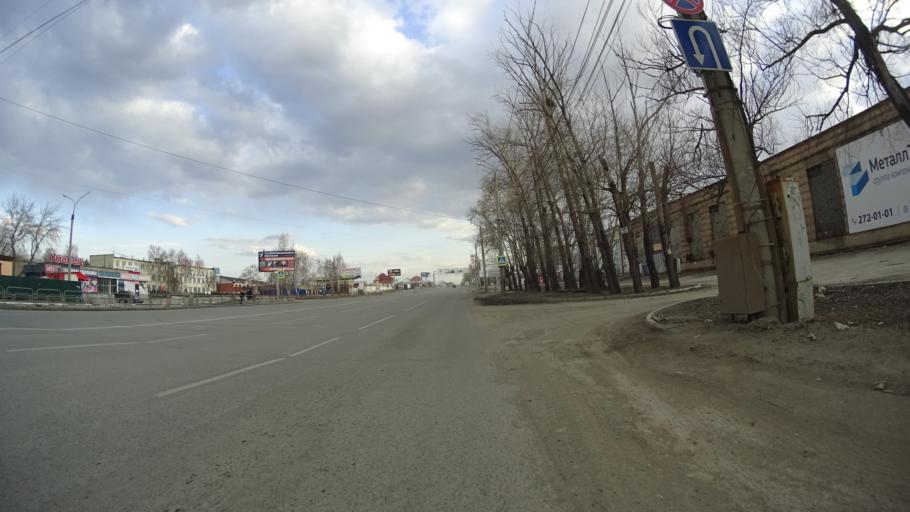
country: RU
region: Chelyabinsk
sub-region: Gorod Chelyabinsk
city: Chelyabinsk
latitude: 55.1128
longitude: 61.3866
